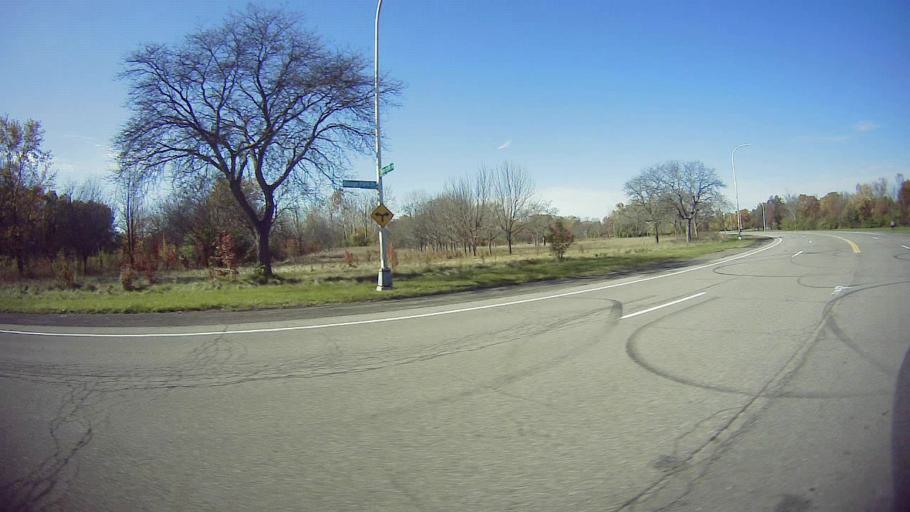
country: US
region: Michigan
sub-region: Wayne County
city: Dearborn Heights
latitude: 42.3684
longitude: -83.2560
